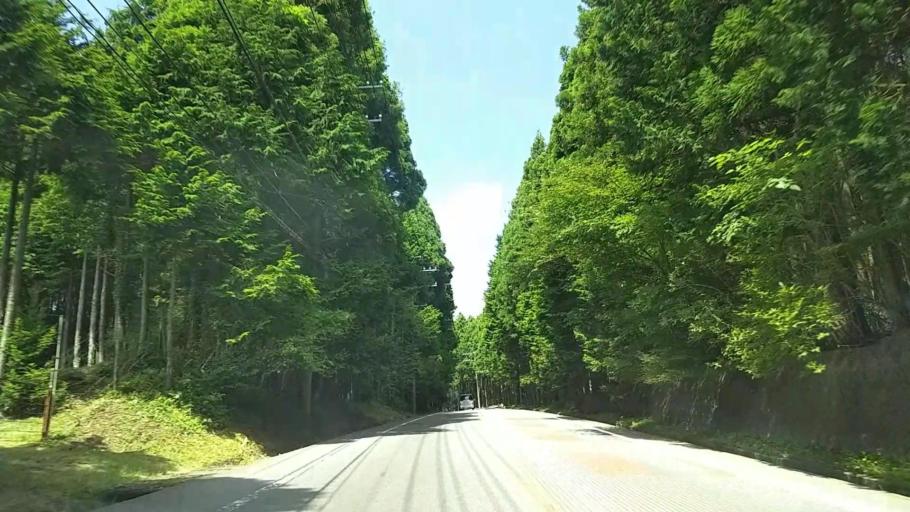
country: JP
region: Shizuoka
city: Gotemba
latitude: 35.2593
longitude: 138.8211
